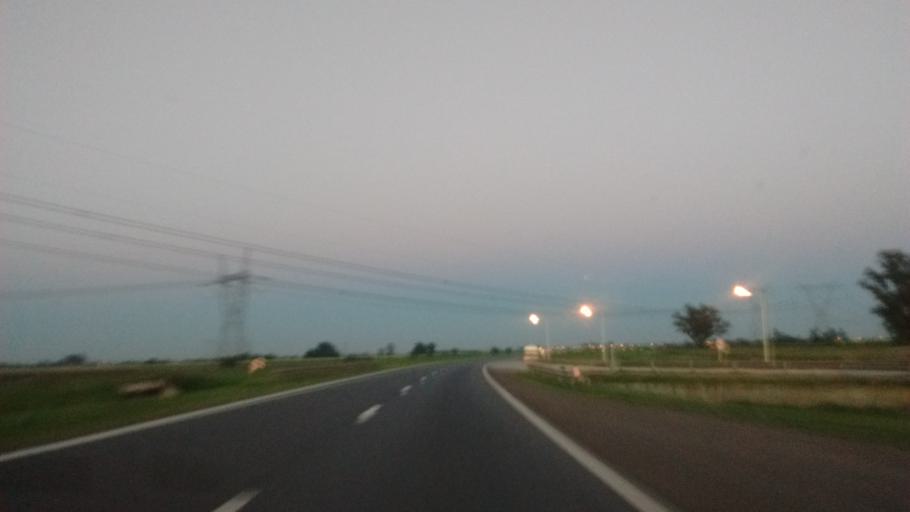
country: AR
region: Santa Fe
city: Roldan
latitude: -32.9245
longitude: -60.9120
